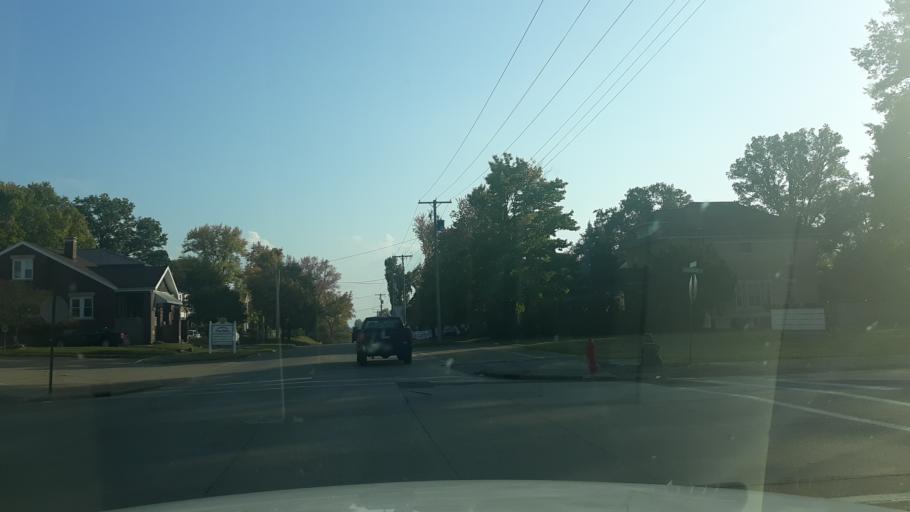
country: US
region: Illinois
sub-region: Saline County
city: Harrisburg
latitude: 37.7372
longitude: -88.5403
